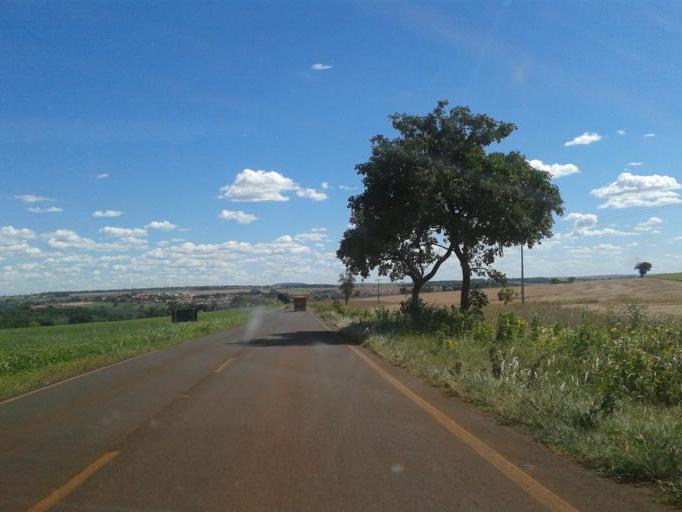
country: BR
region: Minas Gerais
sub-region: Capinopolis
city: Capinopolis
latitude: -18.6626
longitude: -49.5577
